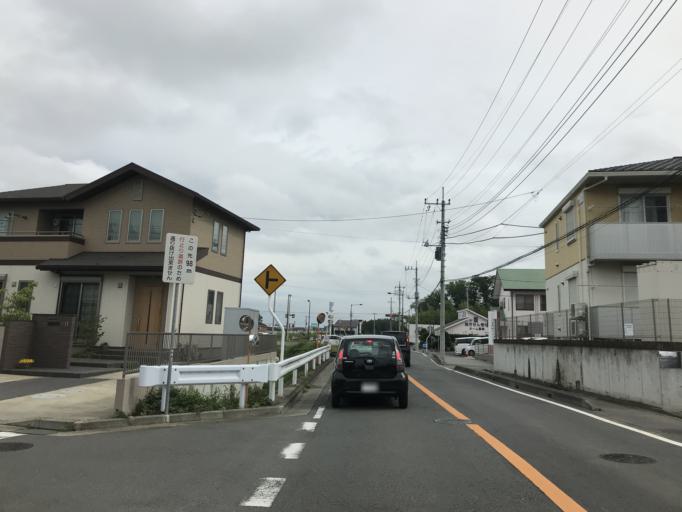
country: JP
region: Ibaraki
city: Mito-shi
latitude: 36.3357
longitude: 140.4588
